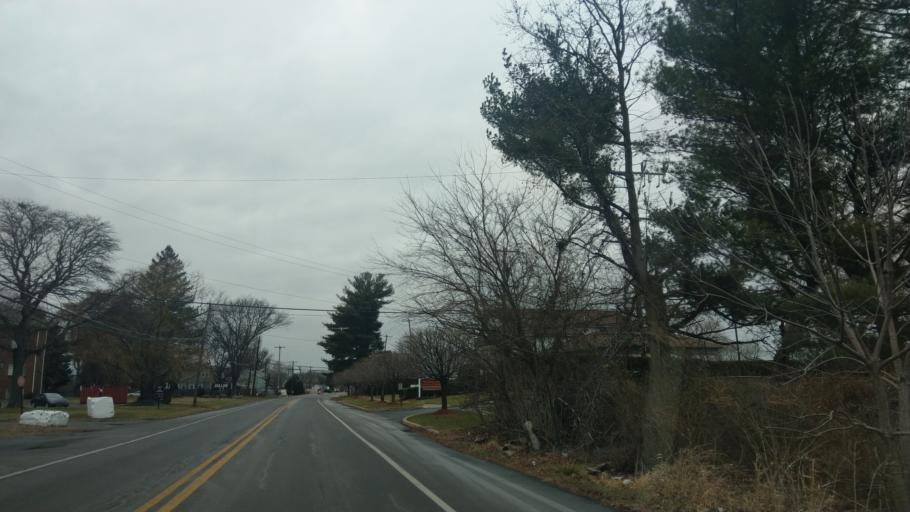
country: US
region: Pennsylvania
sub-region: Bucks County
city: Bristol
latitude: 40.1311
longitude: -74.8699
